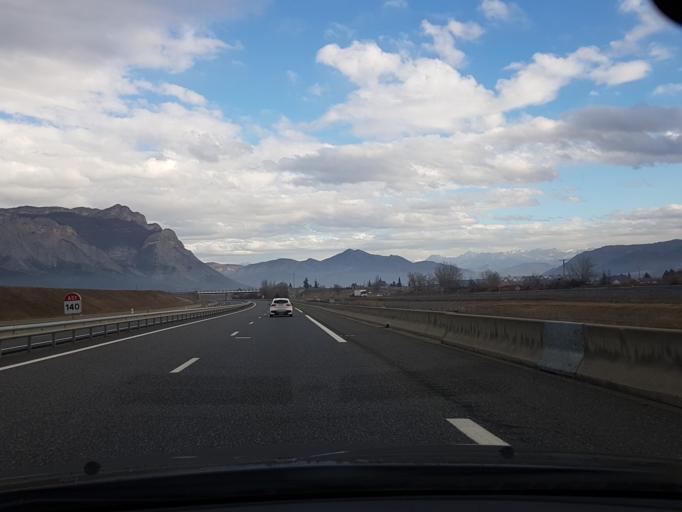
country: FR
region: Provence-Alpes-Cote d'Azur
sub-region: Departement des Hautes-Alpes
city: Laragne-Monteglin
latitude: 44.3630
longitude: 5.9208
